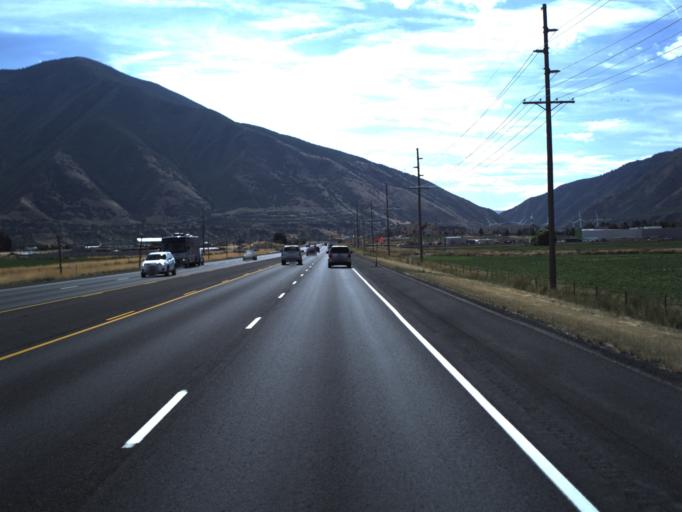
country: US
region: Utah
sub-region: Utah County
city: Spanish Fork
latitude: 40.1022
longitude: -111.6180
